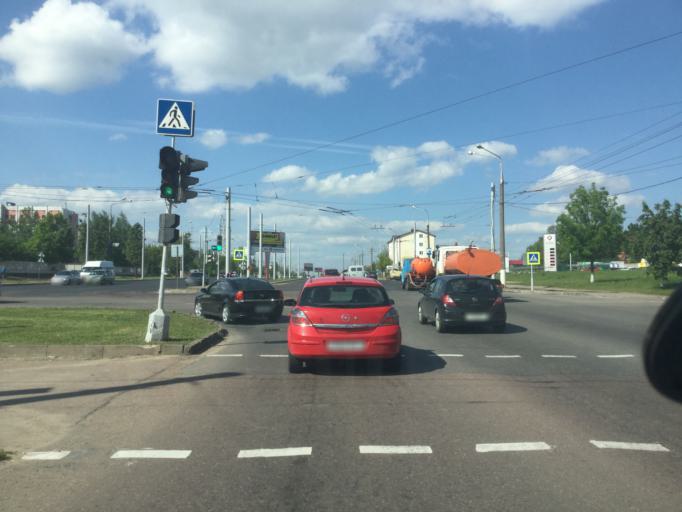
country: BY
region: Vitebsk
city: Vitebsk
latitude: 55.1808
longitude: 30.2471
